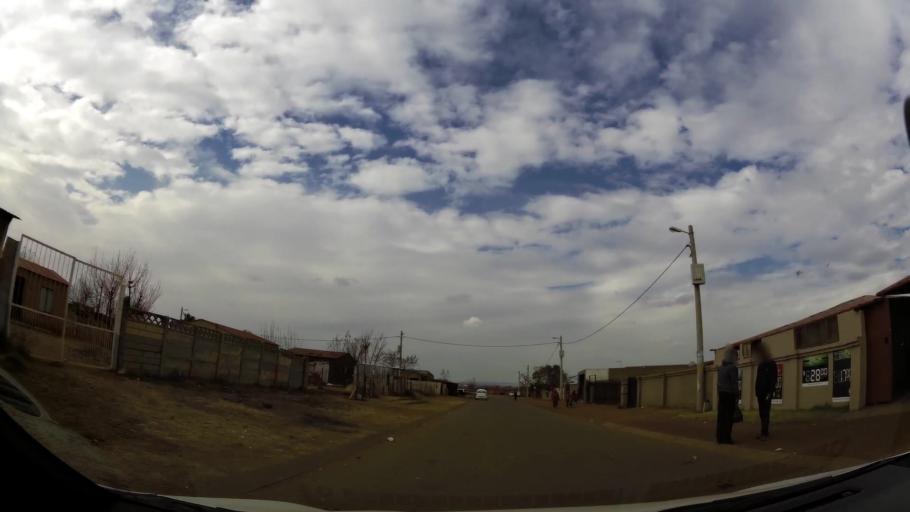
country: ZA
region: Gauteng
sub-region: Ekurhuleni Metropolitan Municipality
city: Germiston
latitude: -26.3972
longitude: 28.1537
